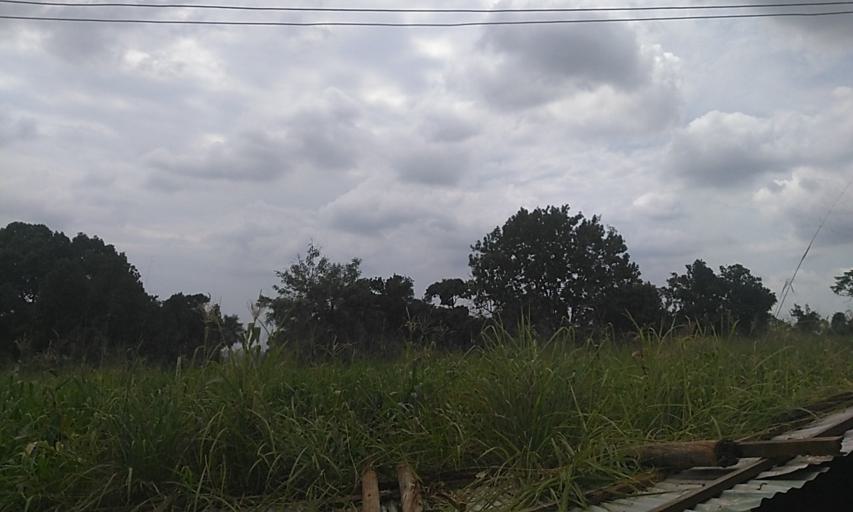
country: UG
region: Central Region
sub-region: Kampala District
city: Kampala
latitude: 0.3339
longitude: 32.6118
